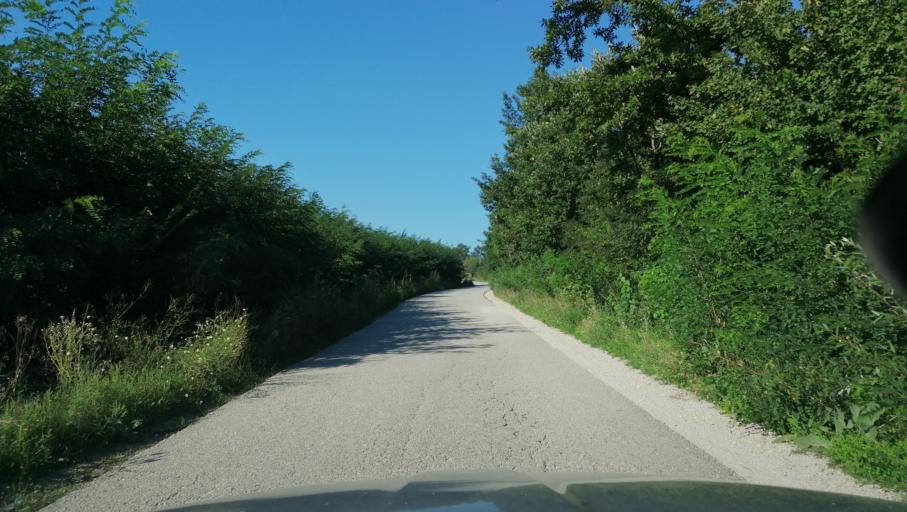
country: RS
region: Central Serbia
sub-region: Sumadijski Okrug
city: Knic
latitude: 43.8644
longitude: 20.6032
